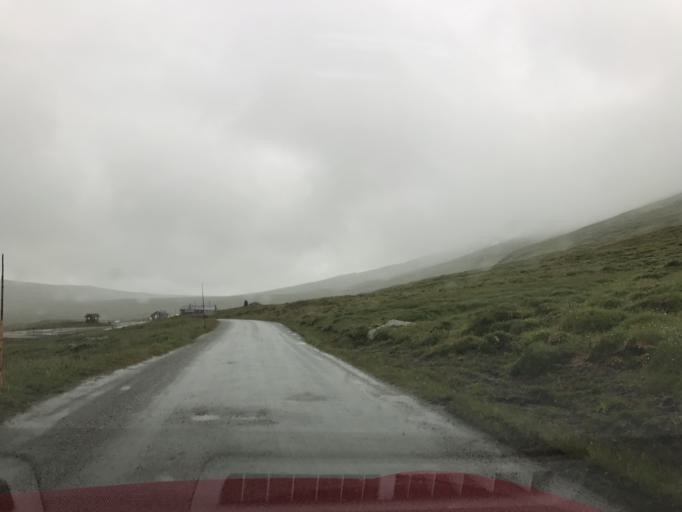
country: NO
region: Buskerud
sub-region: Hol
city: Geilo
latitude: 60.5510
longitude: 8.0730
